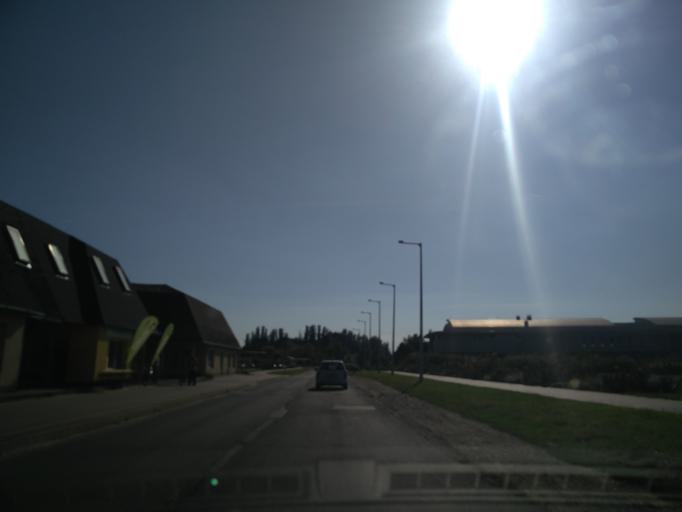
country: HU
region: Fejer
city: Velence
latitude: 47.2278
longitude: 18.6627
